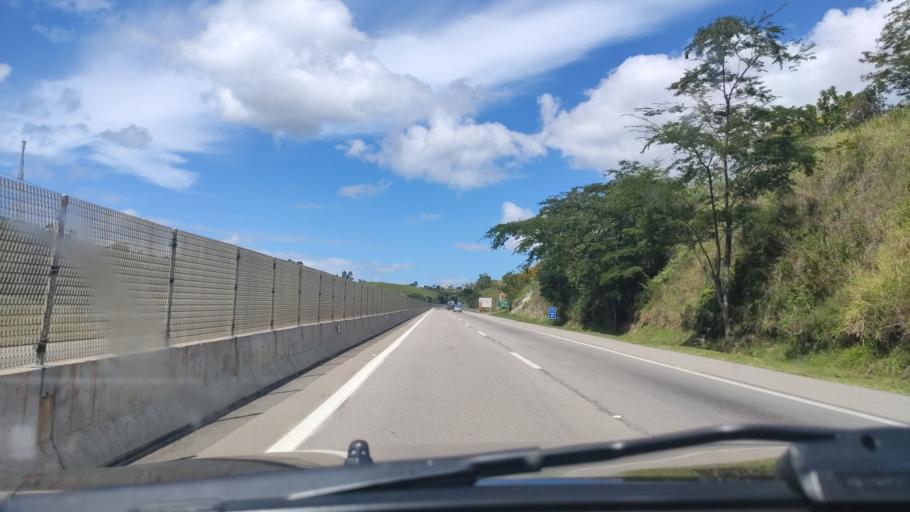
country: BR
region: Sao Paulo
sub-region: Santa Branca
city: Santa Branca
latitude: -23.4303
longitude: -45.6236
